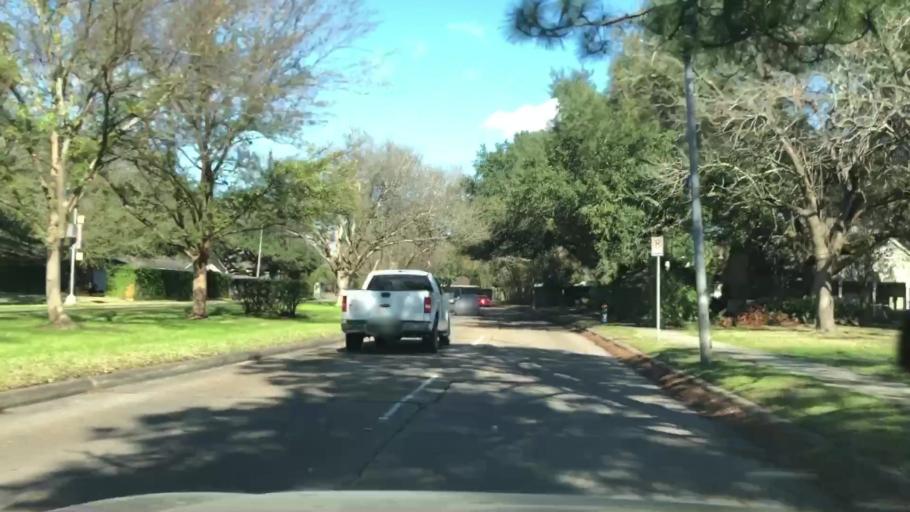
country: US
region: Texas
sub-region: Harris County
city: Bellaire
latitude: 29.6708
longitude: -95.4922
